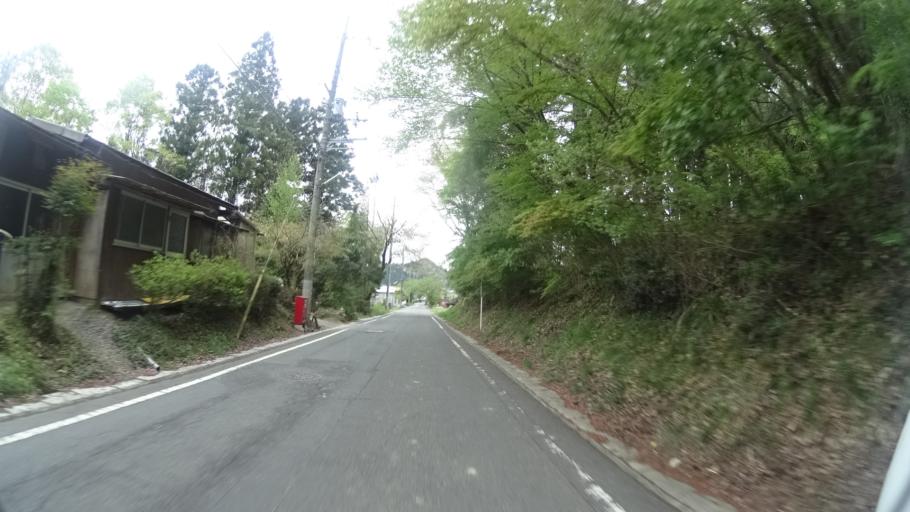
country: JP
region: Kyoto
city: Kameoka
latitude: 35.1996
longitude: 135.4621
